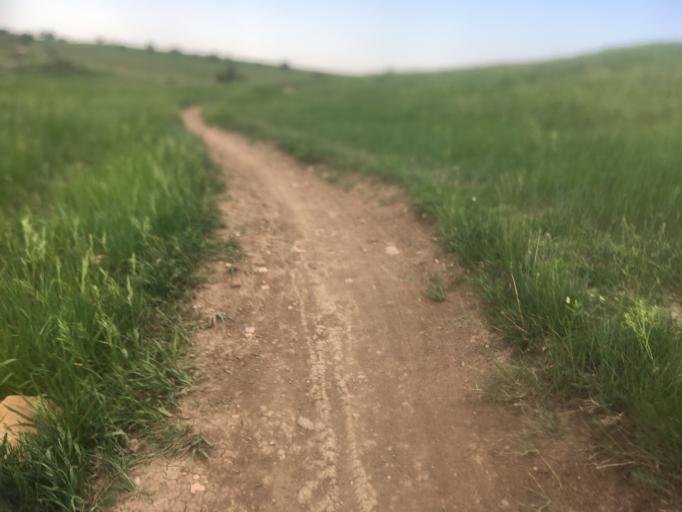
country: US
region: Colorado
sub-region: Boulder County
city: Superior
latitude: 39.9591
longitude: -105.2023
